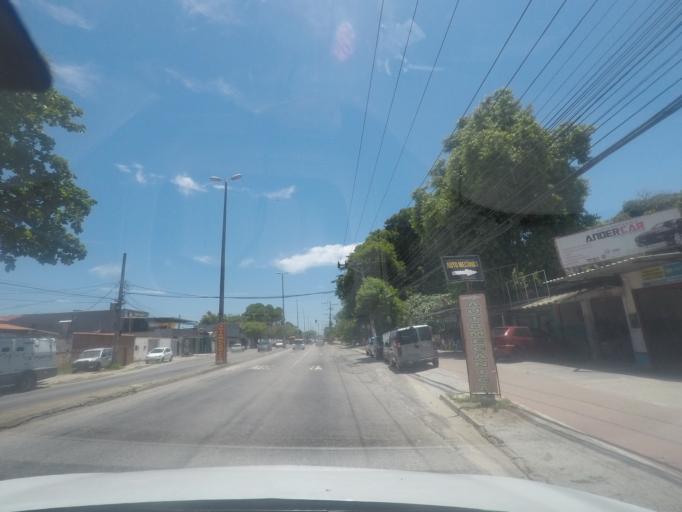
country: BR
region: Rio de Janeiro
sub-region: Itaguai
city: Itaguai
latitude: -22.9057
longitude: -43.6841
